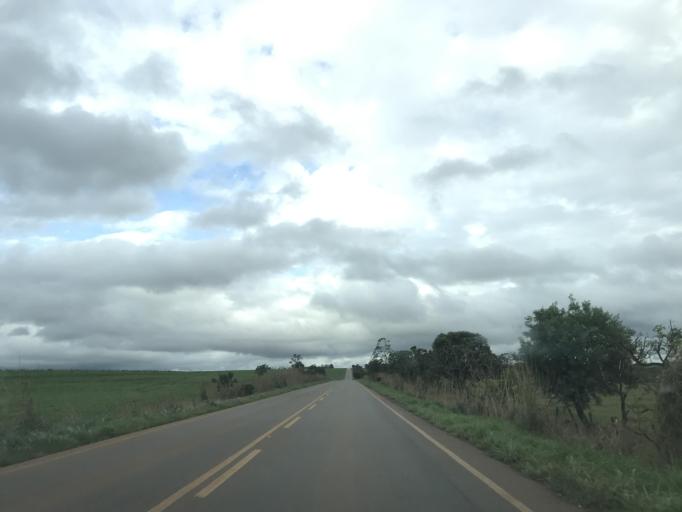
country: BR
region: Goias
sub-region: Vianopolis
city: Vianopolis
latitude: -16.5637
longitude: -48.2877
